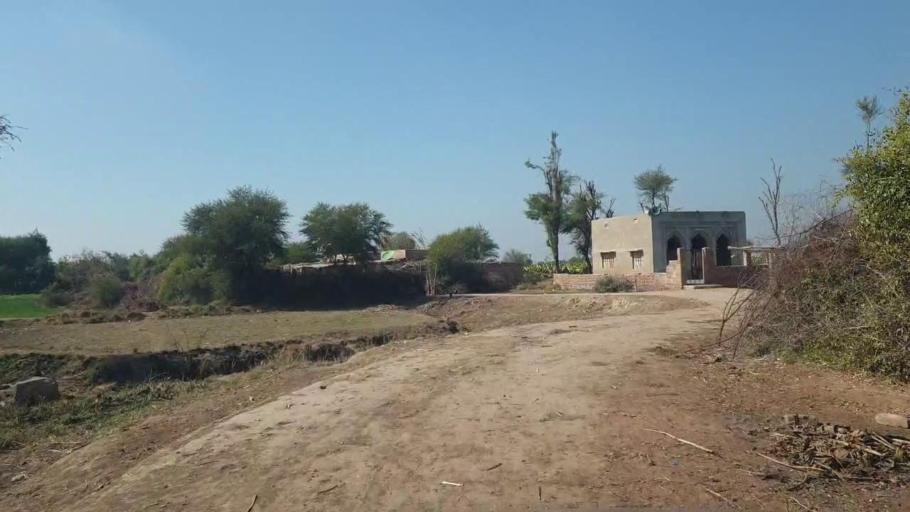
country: PK
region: Sindh
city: Shahdadpur
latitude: 25.9315
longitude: 68.5811
